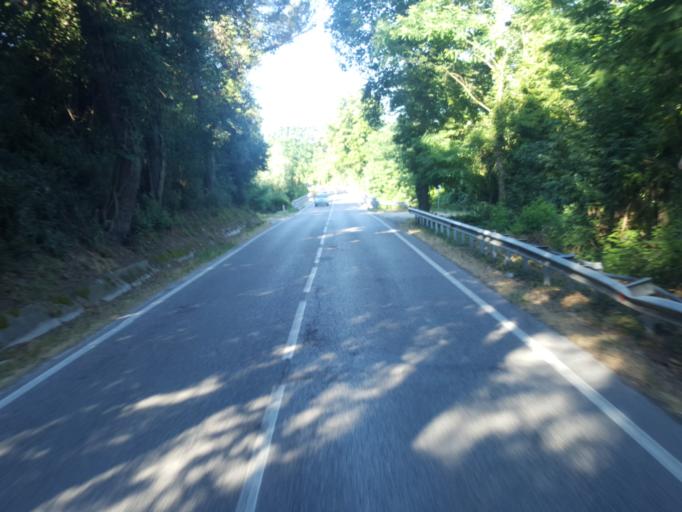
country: IT
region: The Marches
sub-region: Provincia di Pesaro e Urbino
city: Padiglione
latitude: 43.8449
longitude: 12.7123
